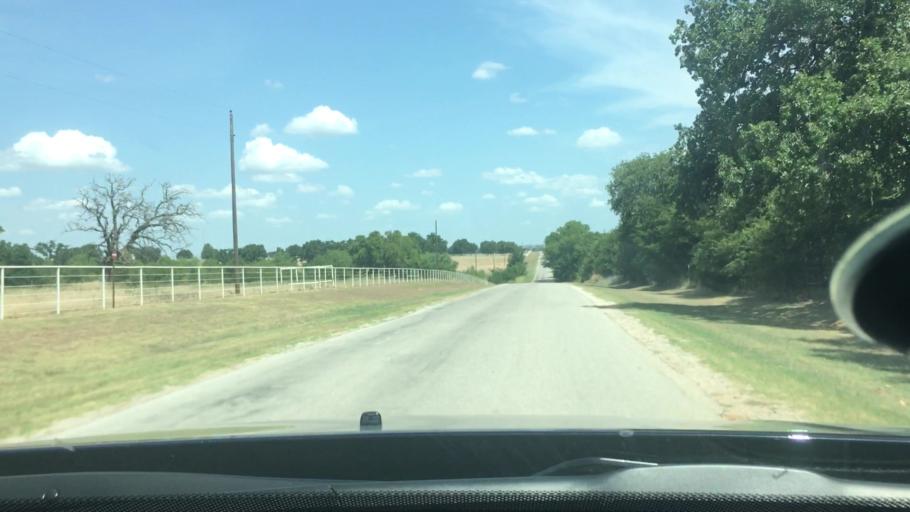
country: US
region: Oklahoma
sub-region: Love County
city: Marietta
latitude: 34.0381
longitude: -97.1957
